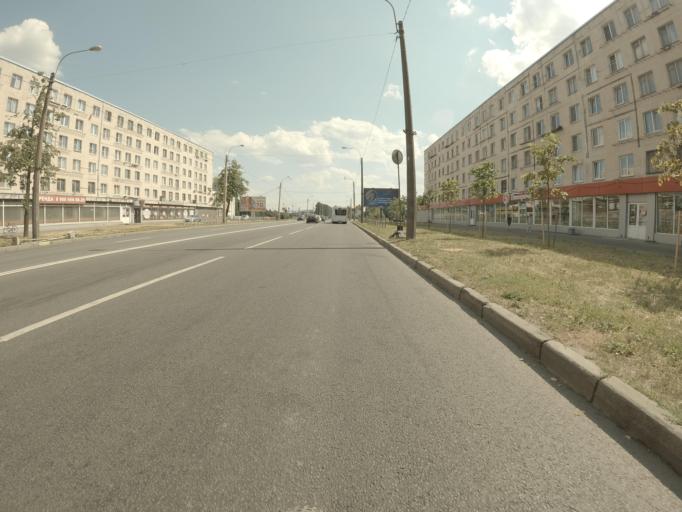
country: RU
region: St.-Petersburg
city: Avtovo
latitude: 59.8676
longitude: 30.2752
